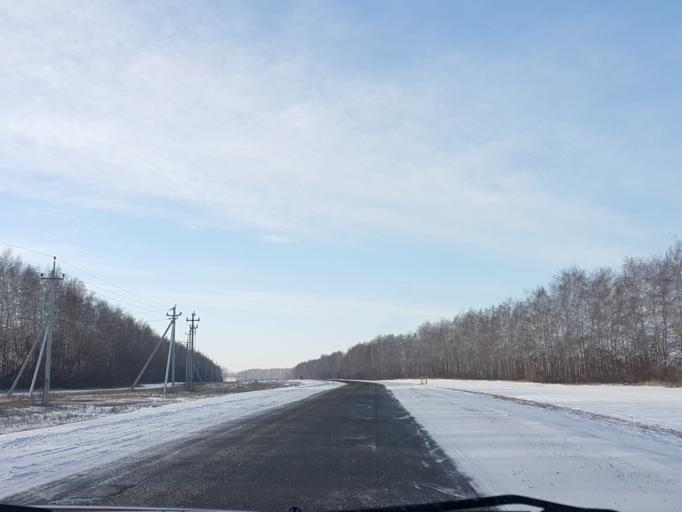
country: RU
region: Tambov
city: Znamenka
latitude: 52.3789
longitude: 41.3164
